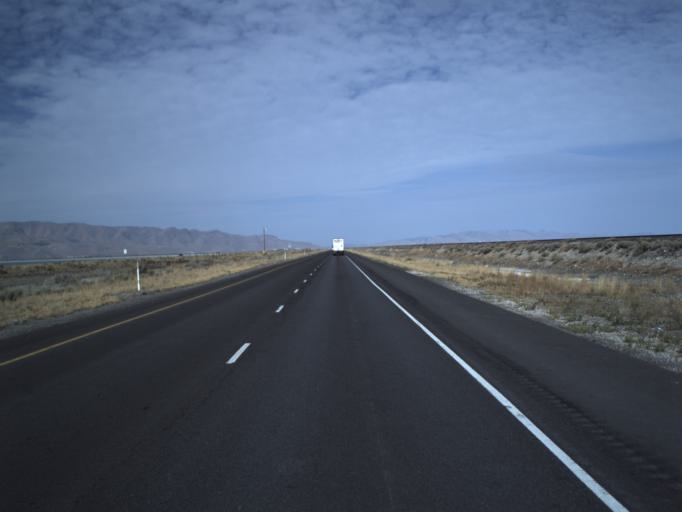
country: US
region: Utah
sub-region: Tooele County
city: Stansbury park
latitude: 40.6683
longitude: -112.3759
